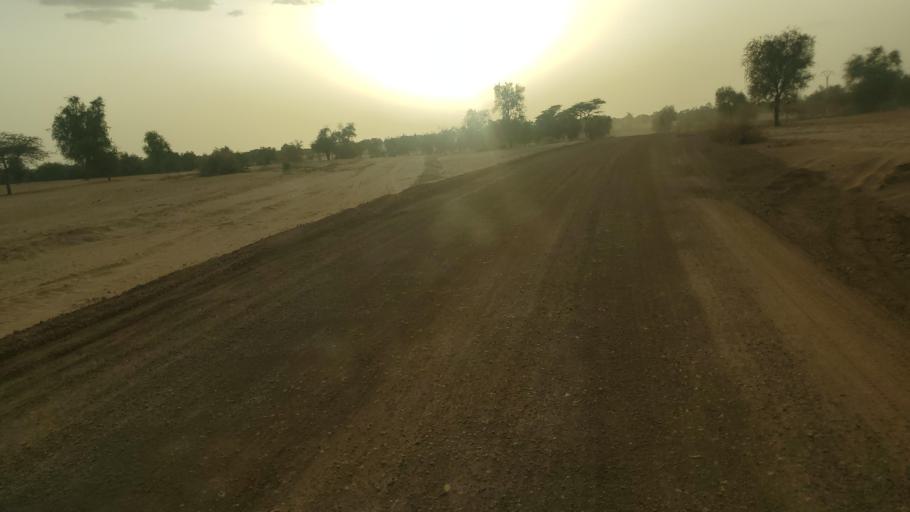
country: SN
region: Louga
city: Dara
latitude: 15.3784
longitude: -15.6005
